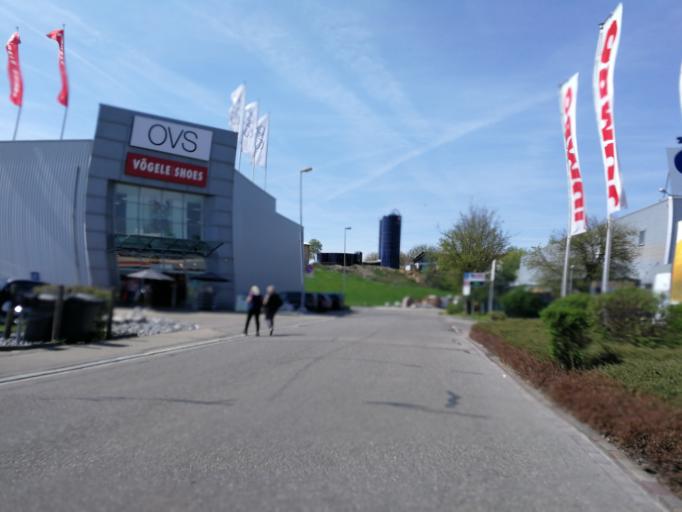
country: CH
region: Zurich
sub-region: Bezirk Hinwil
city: Wetzikon / Ober-Wetzikon
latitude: 47.3063
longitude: 8.8169
